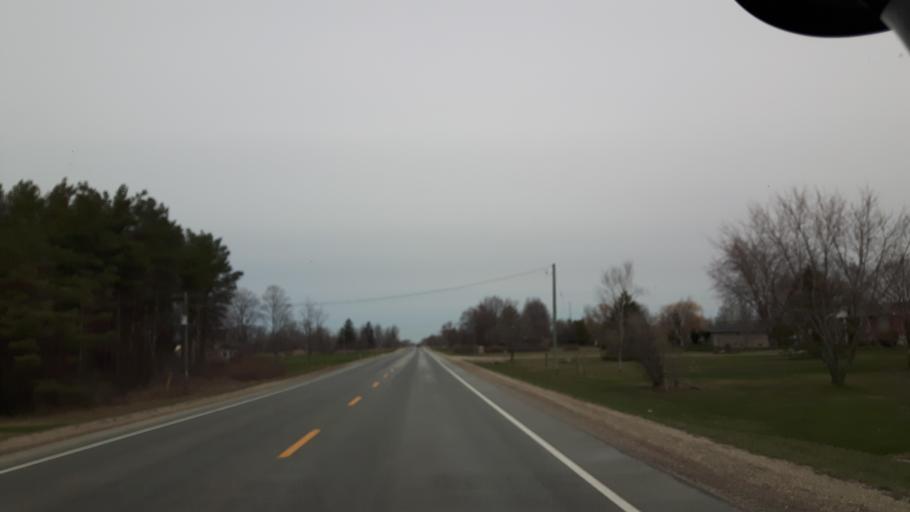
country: CA
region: Ontario
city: Goderich
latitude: 43.7087
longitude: -81.7056
